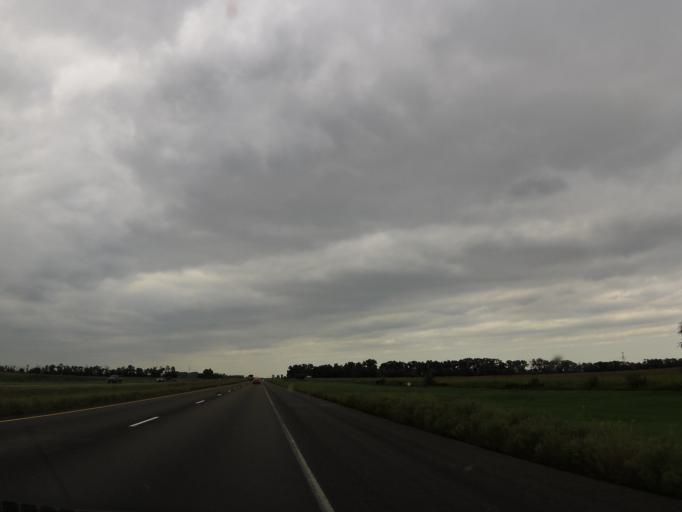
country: US
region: North Dakota
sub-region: Richland County
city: Wahpeton
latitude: 46.0879
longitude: -96.8355
